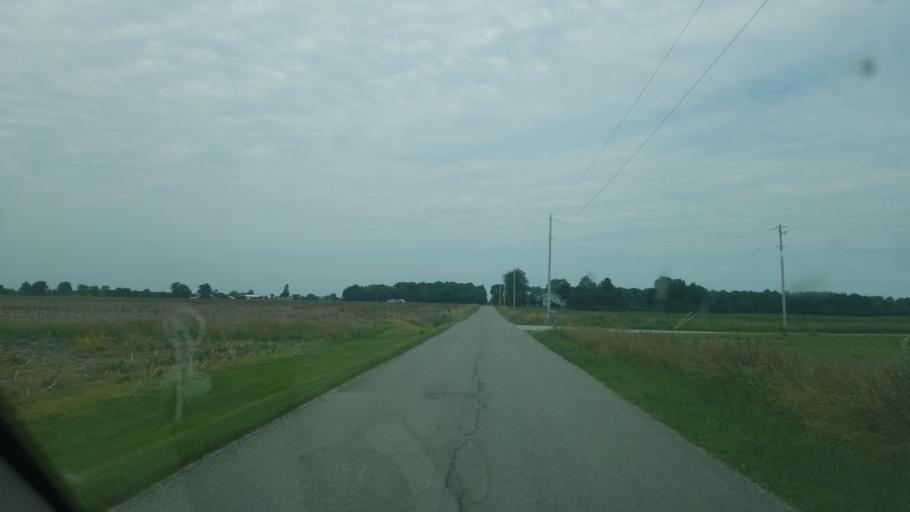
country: US
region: Ohio
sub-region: Seneca County
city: Fostoria
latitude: 41.0502
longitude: -83.4480
